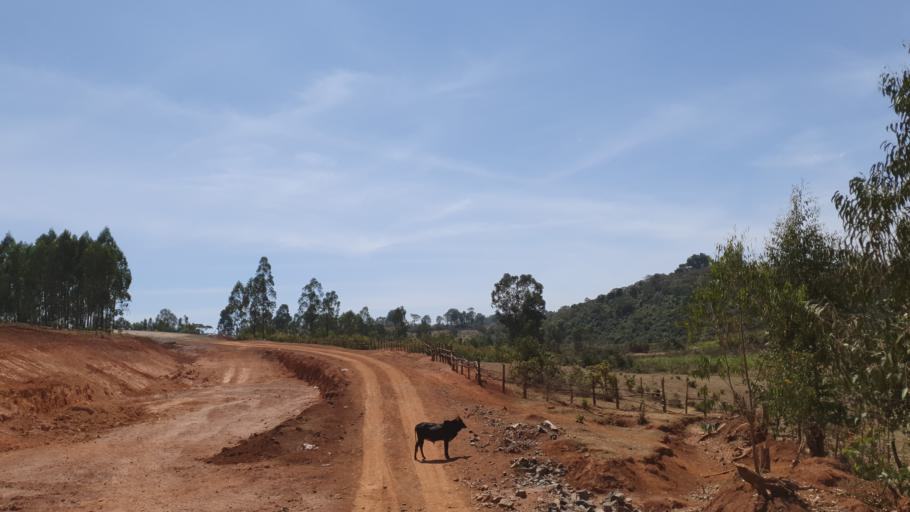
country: ET
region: Oromiya
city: Shambu
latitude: 9.8875
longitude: 36.6499
